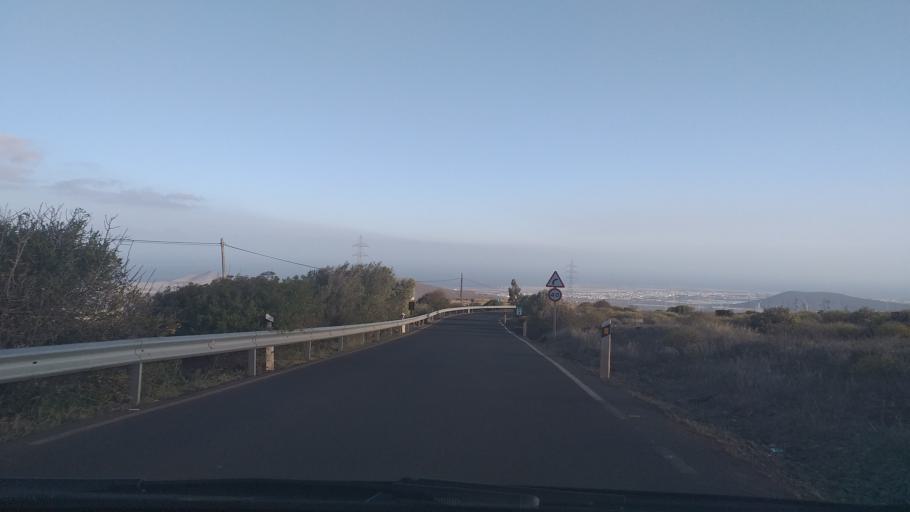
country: ES
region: Canary Islands
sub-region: Provincia de Las Palmas
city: Ingenio
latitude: 27.9299
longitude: -15.4566
